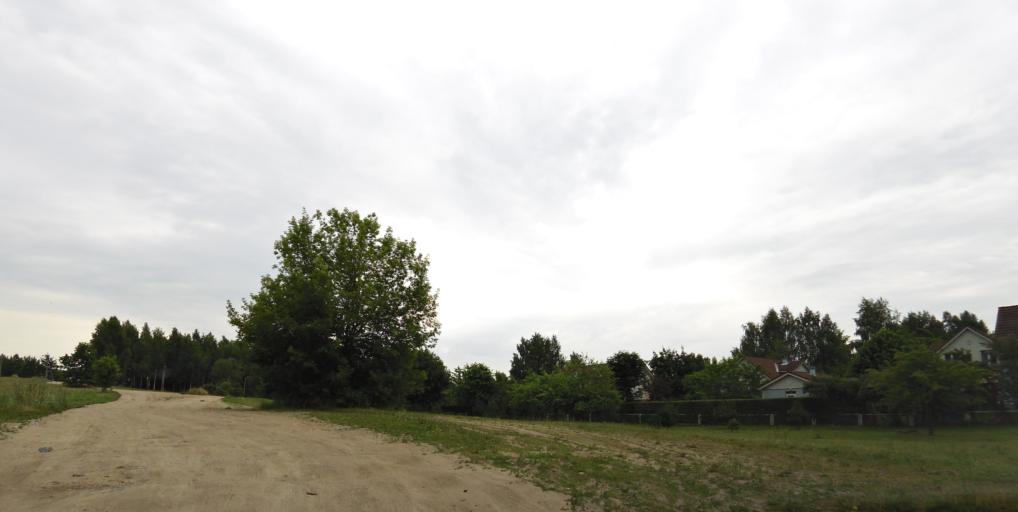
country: LT
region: Vilnius County
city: Seskine
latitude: 54.7057
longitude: 25.2405
